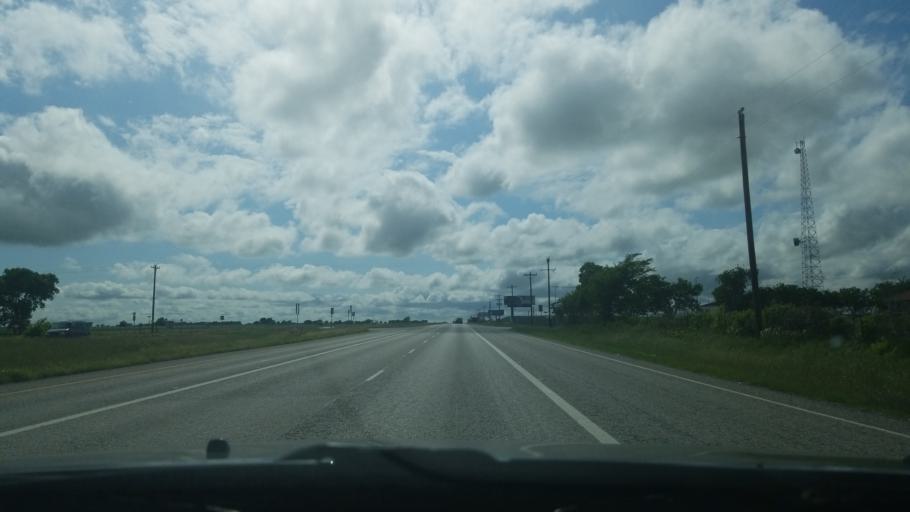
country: US
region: Texas
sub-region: Denton County
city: Ponder
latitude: 33.2386
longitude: -97.3200
